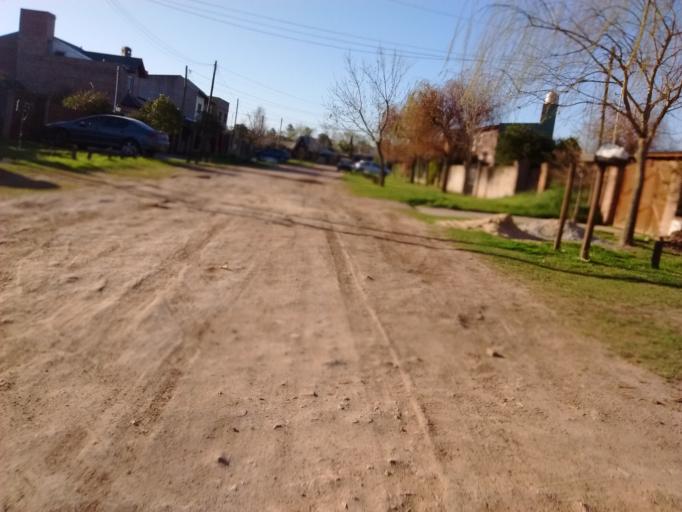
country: AR
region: Santa Fe
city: Funes
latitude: -32.9253
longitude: -60.7944
